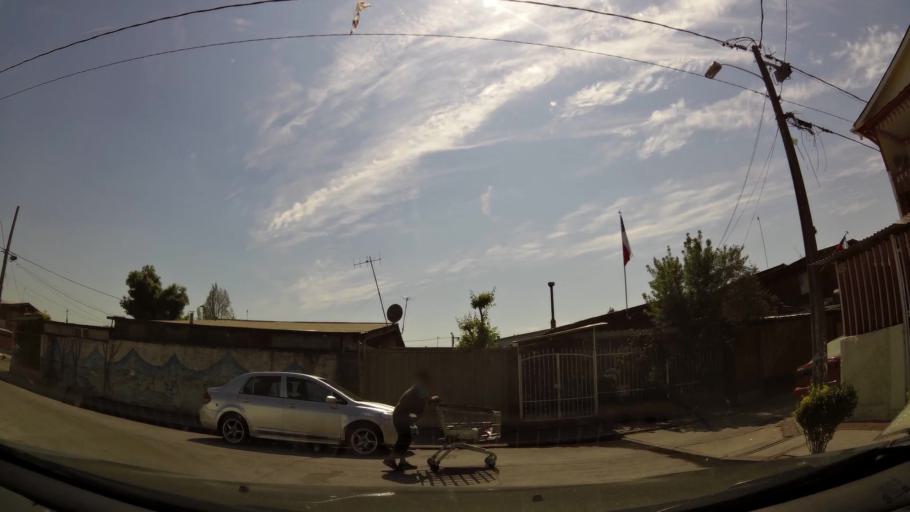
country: CL
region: Santiago Metropolitan
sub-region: Provincia de Santiago
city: La Pintana
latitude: -33.5880
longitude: -70.6127
